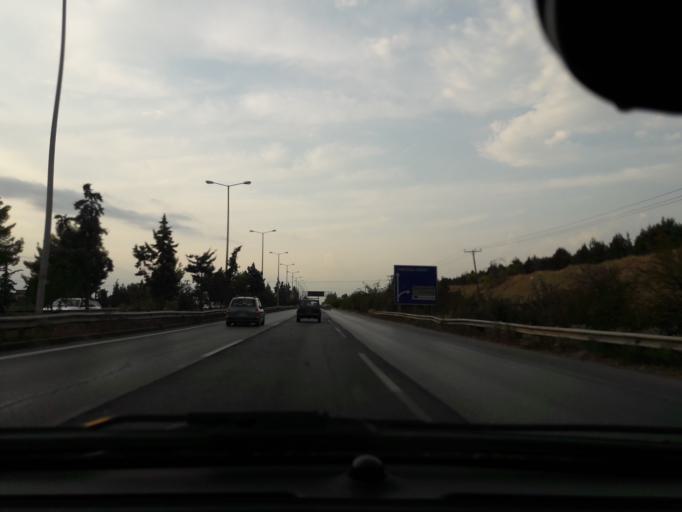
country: GR
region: Central Macedonia
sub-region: Nomos Thessalonikis
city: Pylaia
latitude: 40.5666
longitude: 22.9881
